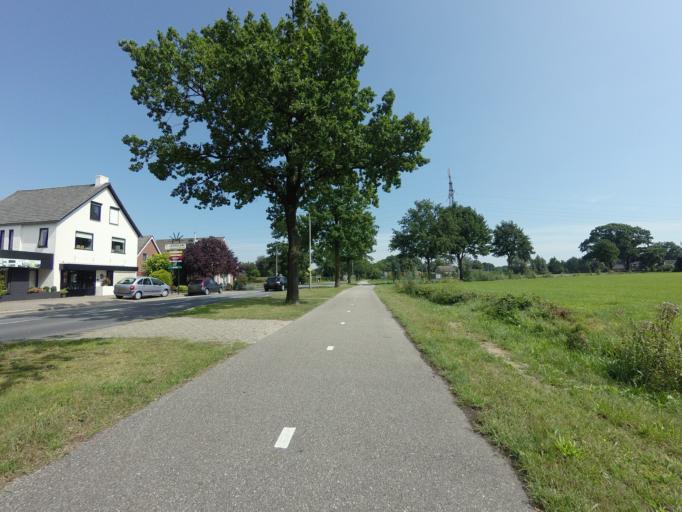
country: NL
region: Overijssel
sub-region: Gemeente Hof van Twente
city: Hengevelde
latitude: 52.2002
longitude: 6.6479
